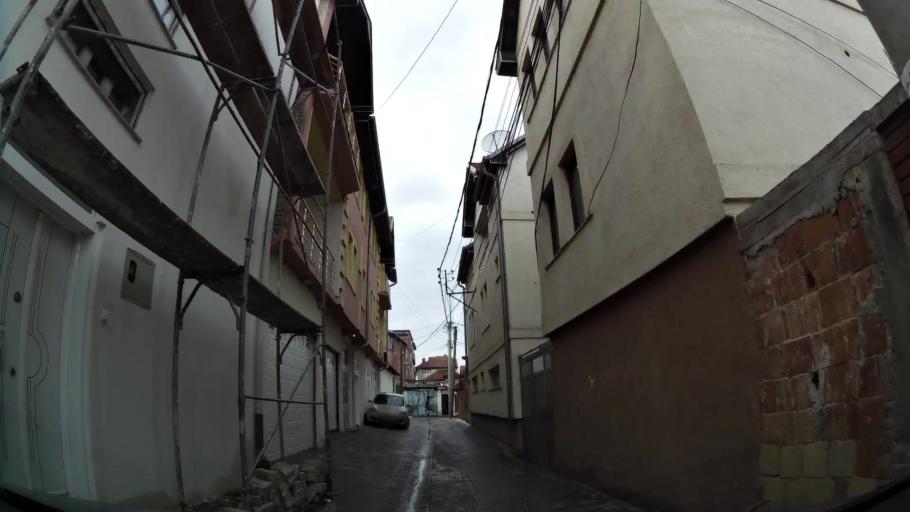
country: XK
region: Pristina
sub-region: Komuna e Prishtines
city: Pristina
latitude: 42.6781
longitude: 21.1626
